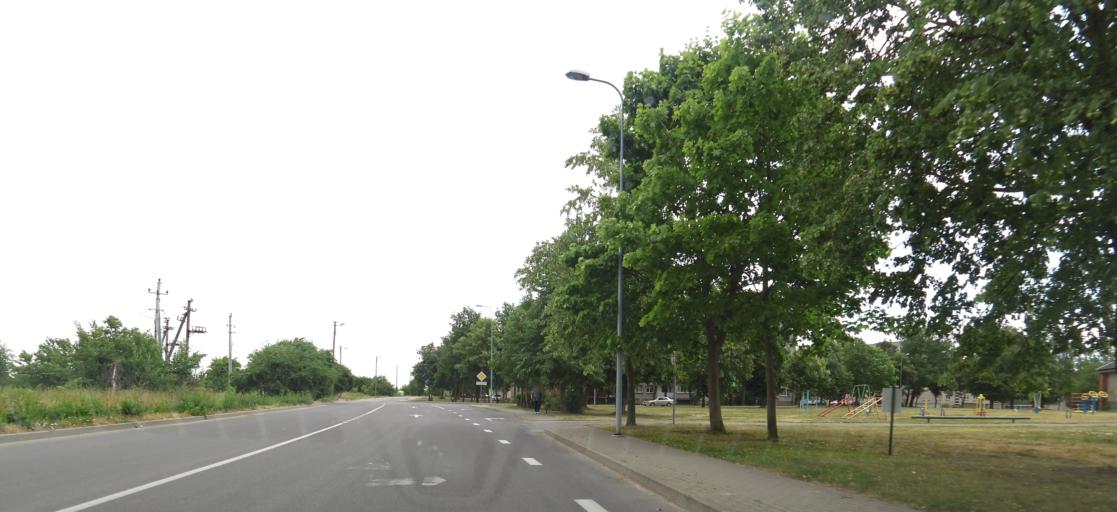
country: LT
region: Vilnius County
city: Ukmerge
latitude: 55.2609
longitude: 24.7775
